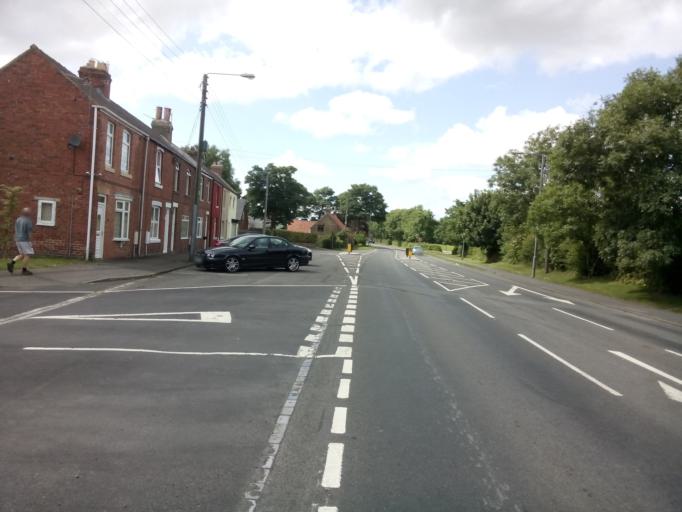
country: GB
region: England
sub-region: County Durham
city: Ushaw Moor
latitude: 54.7710
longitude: -1.6236
